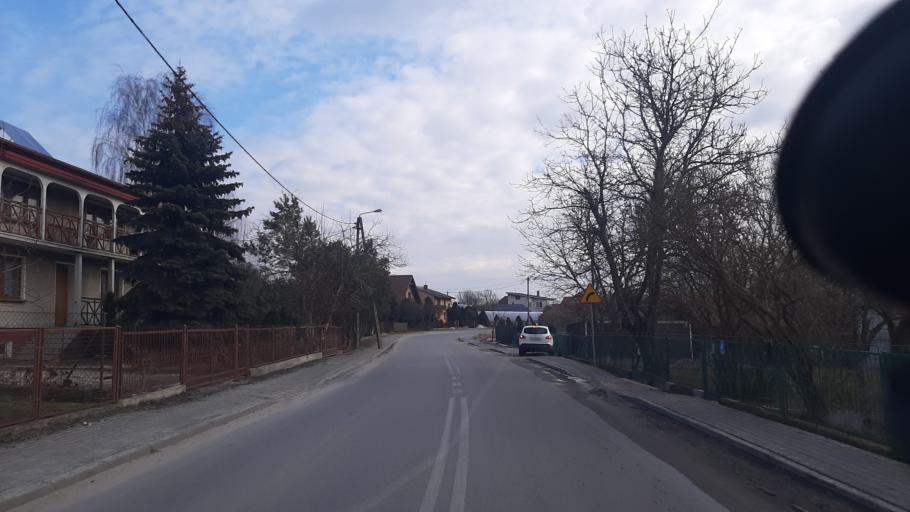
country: PL
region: Lublin Voivodeship
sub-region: Powiat lubartowski
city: Ostrow Lubelski
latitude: 51.4937
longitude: 22.8578
